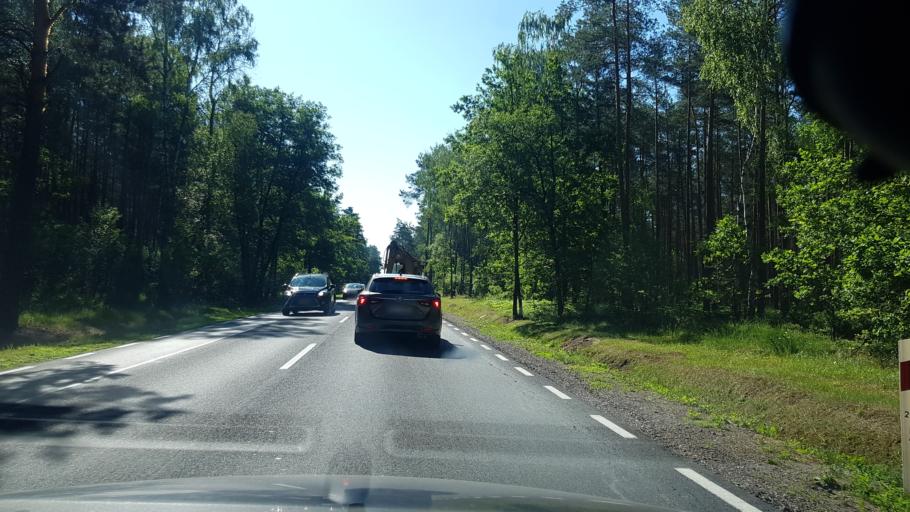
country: PL
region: Masovian Voivodeship
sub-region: Powiat wyszkowski
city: Branszczyk
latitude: 52.5672
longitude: 21.5513
